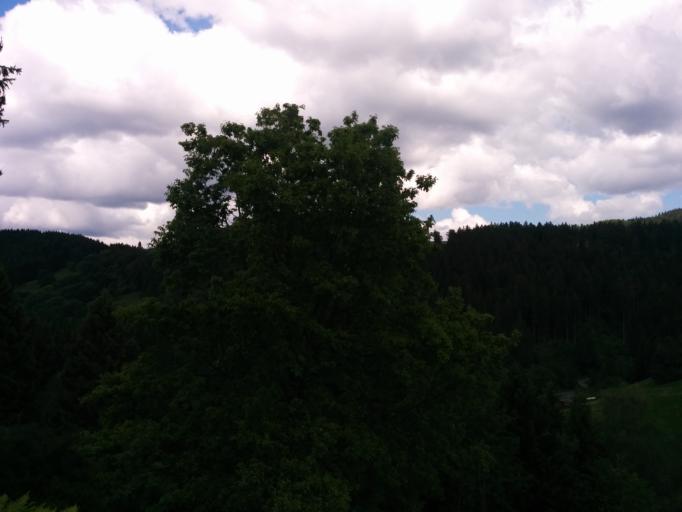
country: DE
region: Lower Saxony
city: Sankt Andreasberg
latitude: 51.7105
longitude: 10.5064
